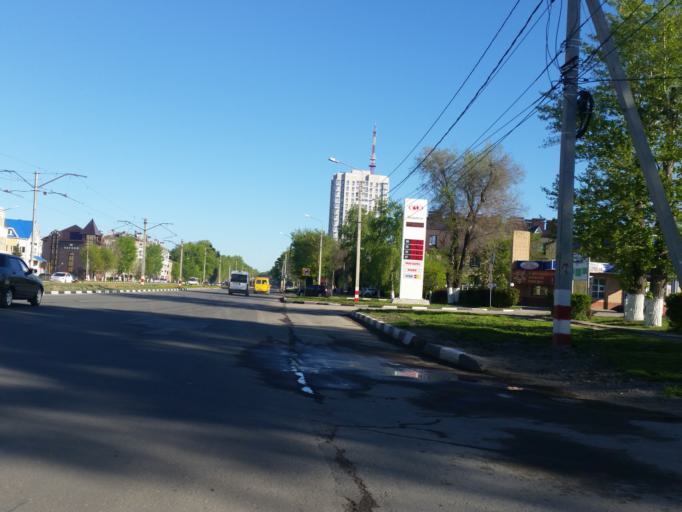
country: RU
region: Ulyanovsk
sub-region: Ulyanovskiy Rayon
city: Ulyanovsk
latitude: 54.3339
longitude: 48.3852
